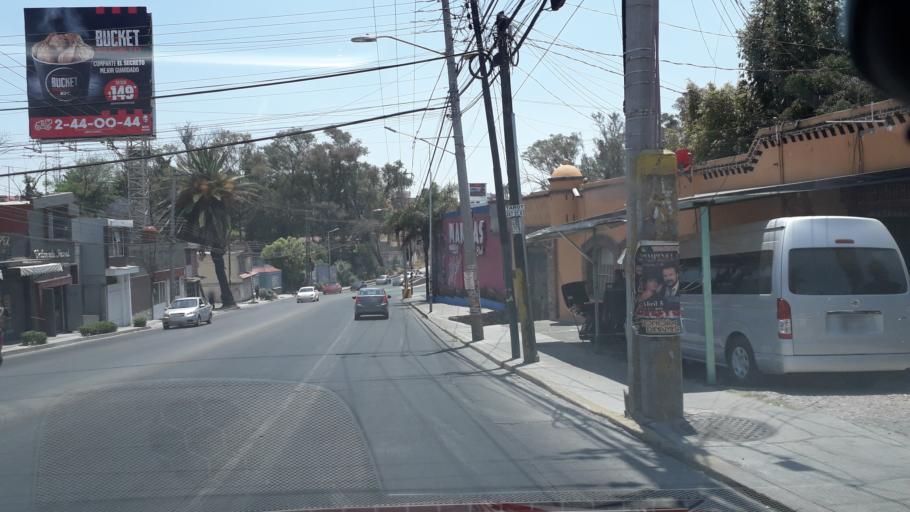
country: MX
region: Puebla
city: Puebla
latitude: 19.0123
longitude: -98.1905
